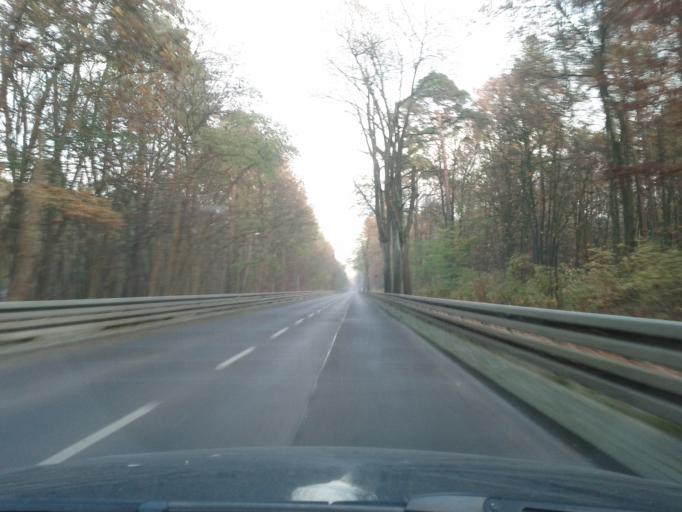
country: DE
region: Berlin
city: Friedrichshagen
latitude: 52.4496
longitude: 13.6530
